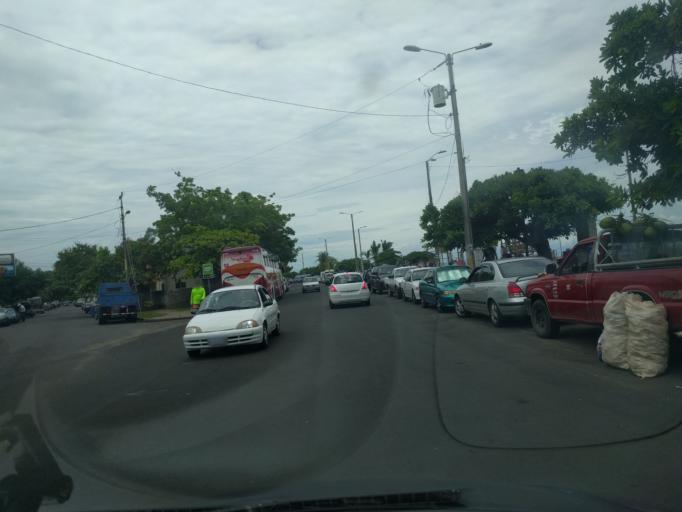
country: CR
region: Puntarenas
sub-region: Canton Central de Puntarenas
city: Puntarenas
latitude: 9.9751
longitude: -84.8488
